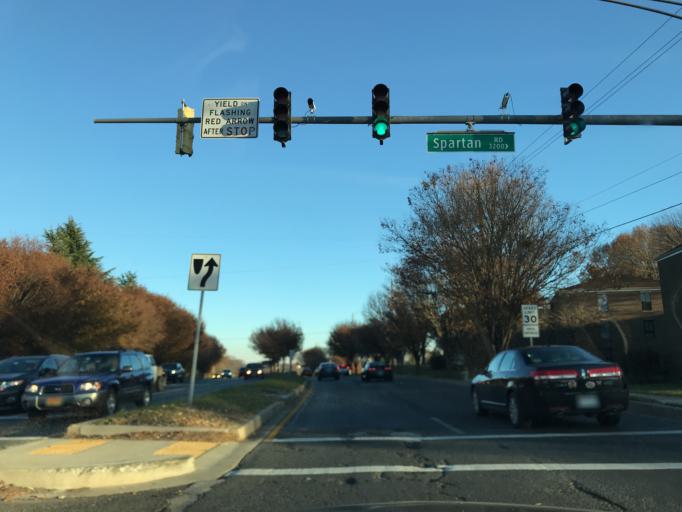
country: US
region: Maryland
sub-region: Montgomery County
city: Olney
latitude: 39.1509
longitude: -77.0623
